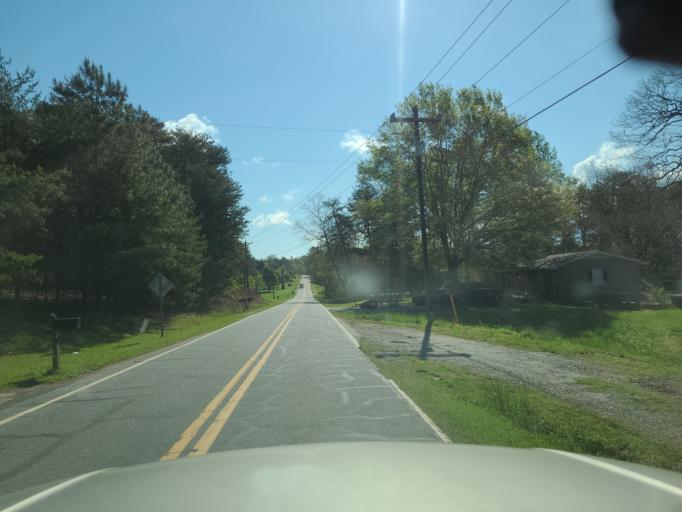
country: US
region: North Carolina
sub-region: Rutherford County
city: Spindale
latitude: 35.2963
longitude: -81.9604
